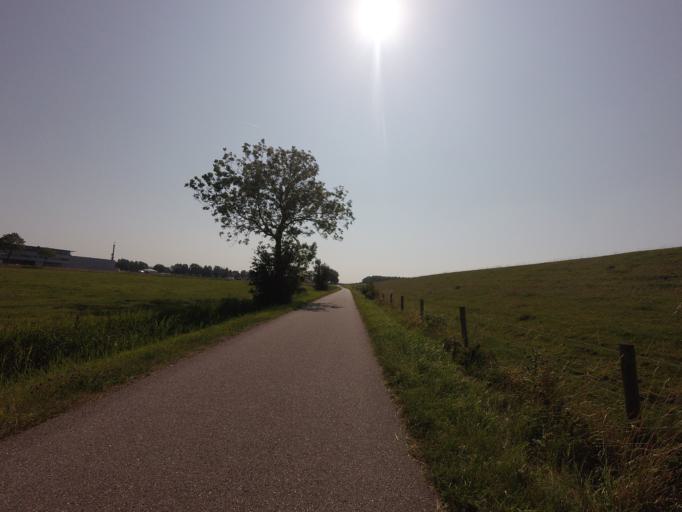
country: NL
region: Groningen
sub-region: Gemeente De Marne
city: Ulrum
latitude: 53.3469
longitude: 6.2973
